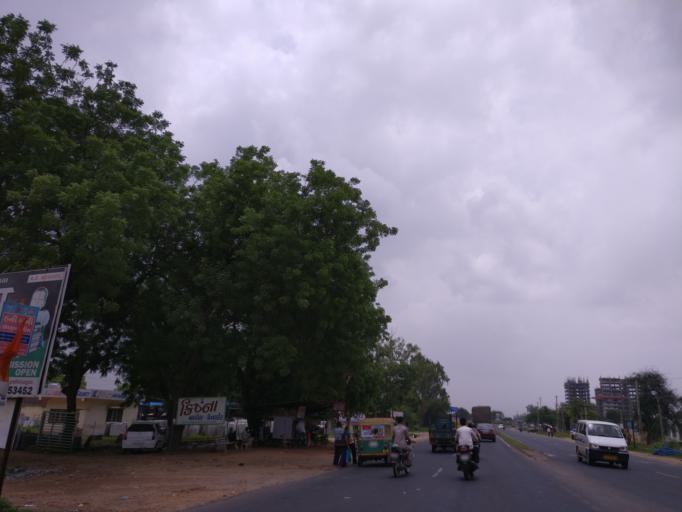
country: IN
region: Gujarat
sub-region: Gandhinagar
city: Adalaj
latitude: 23.1338
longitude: 72.5858
